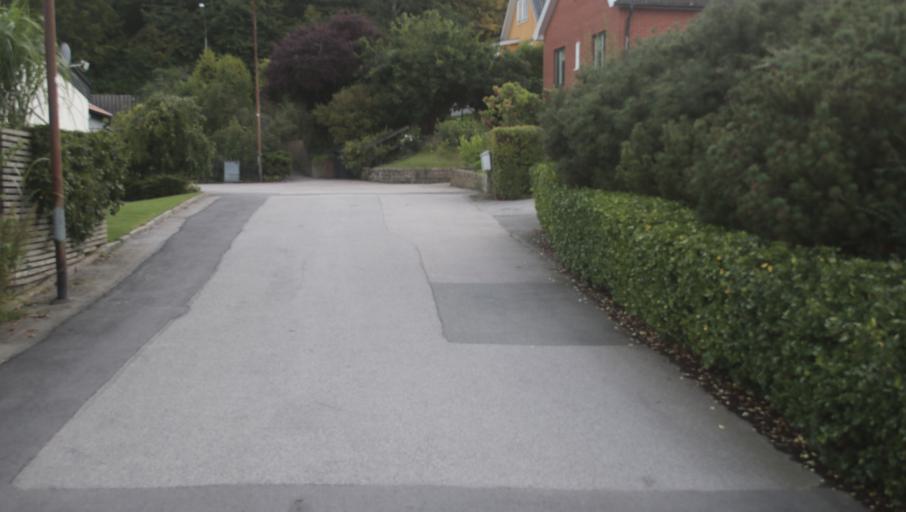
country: SE
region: Blekinge
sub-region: Karlshamns Kommun
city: Karlshamn
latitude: 56.1852
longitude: 14.8621
